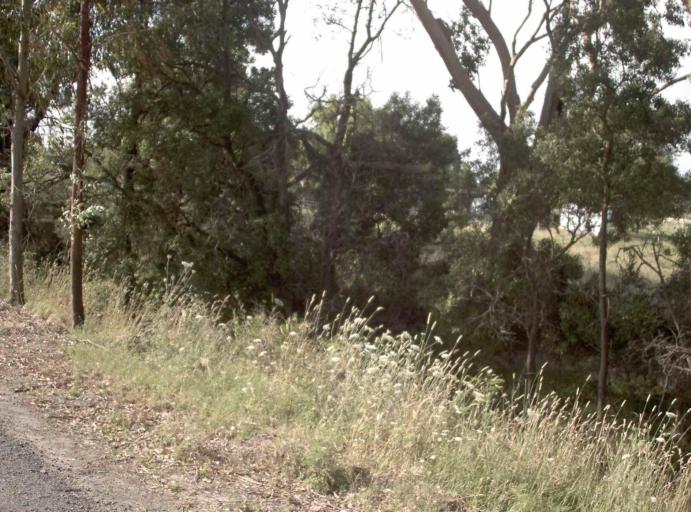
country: AU
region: Victoria
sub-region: Cardinia
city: Bunyip
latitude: -38.1883
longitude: 145.7111
